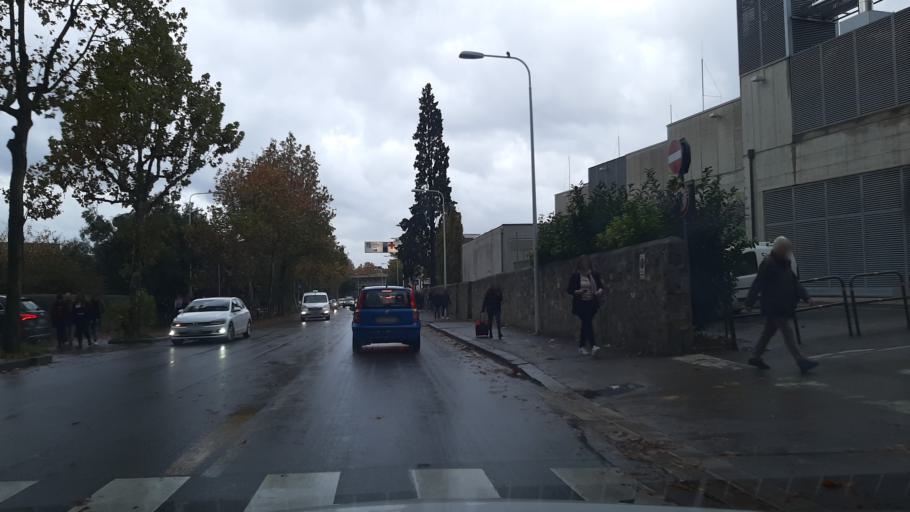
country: IT
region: Tuscany
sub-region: Province of Florence
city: Florence
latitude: 43.8052
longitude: 11.2486
